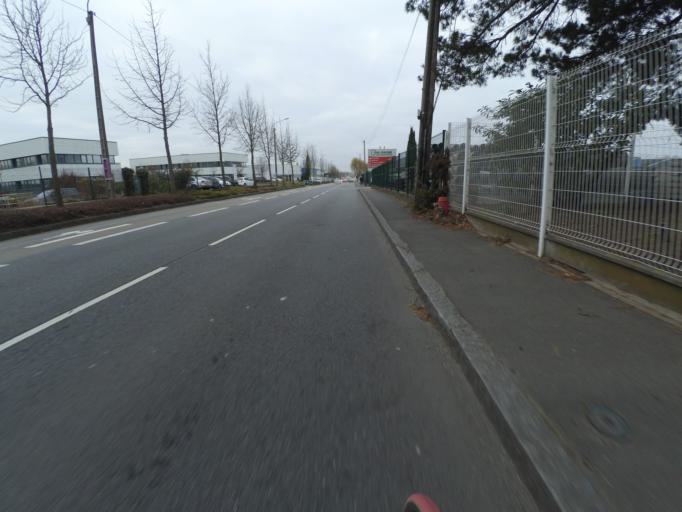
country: FR
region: Pays de la Loire
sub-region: Departement de la Loire-Atlantique
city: Sainte-Luce-sur-Loire
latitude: 47.2666
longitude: -1.4900
